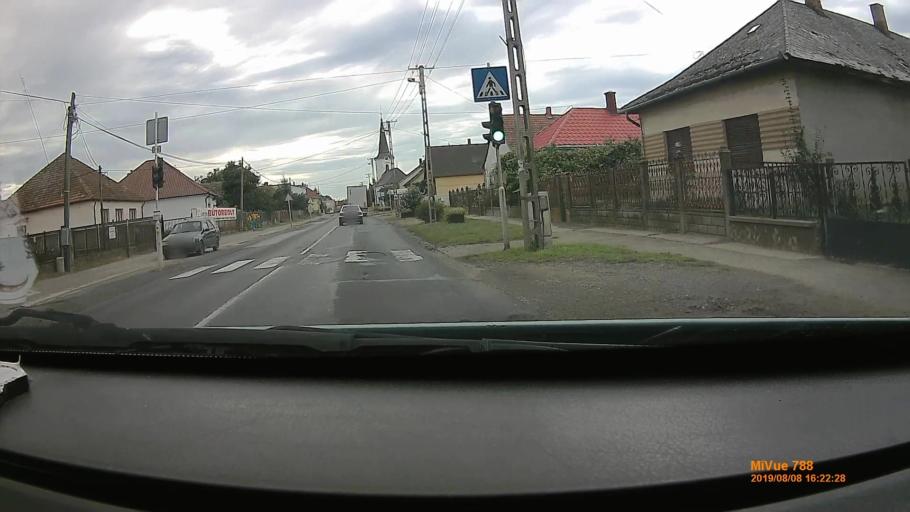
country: HU
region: Szabolcs-Szatmar-Bereg
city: Nyirmeggyes
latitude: 47.9709
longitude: 22.2511
